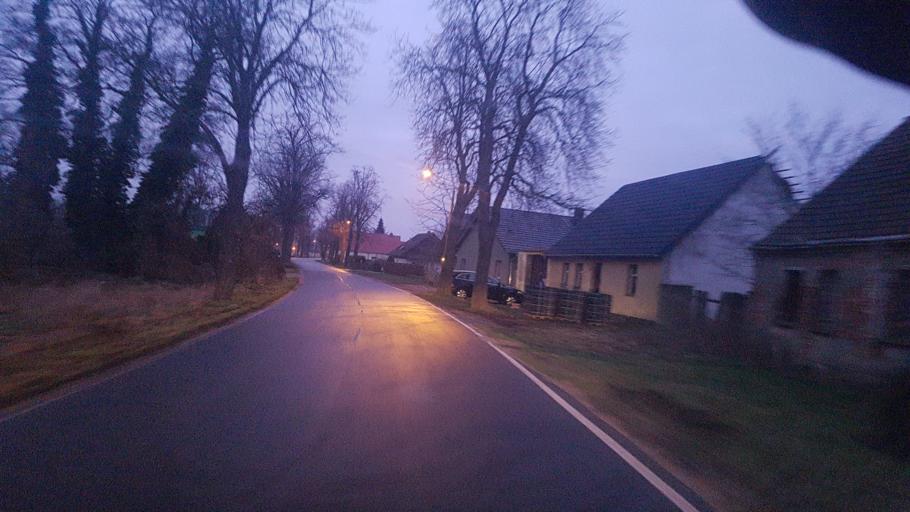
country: DE
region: Brandenburg
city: Luckenwalde
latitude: 52.1042
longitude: 13.1064
